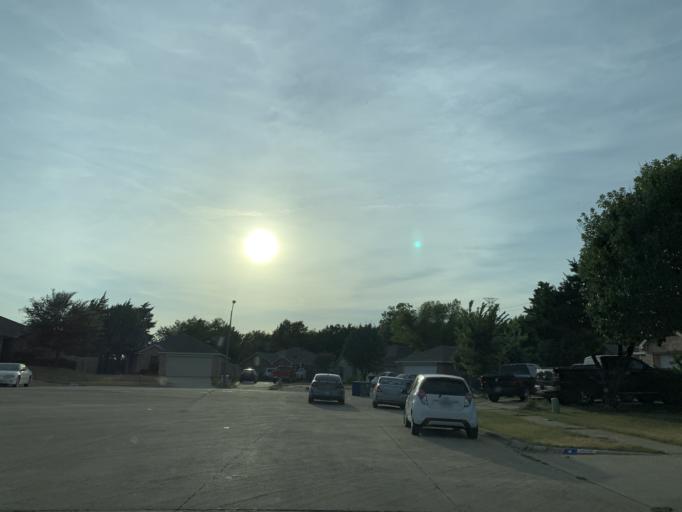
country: US
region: Texas
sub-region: Dallas County
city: Cockrell Hill
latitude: 32.7079
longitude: -96.9043
